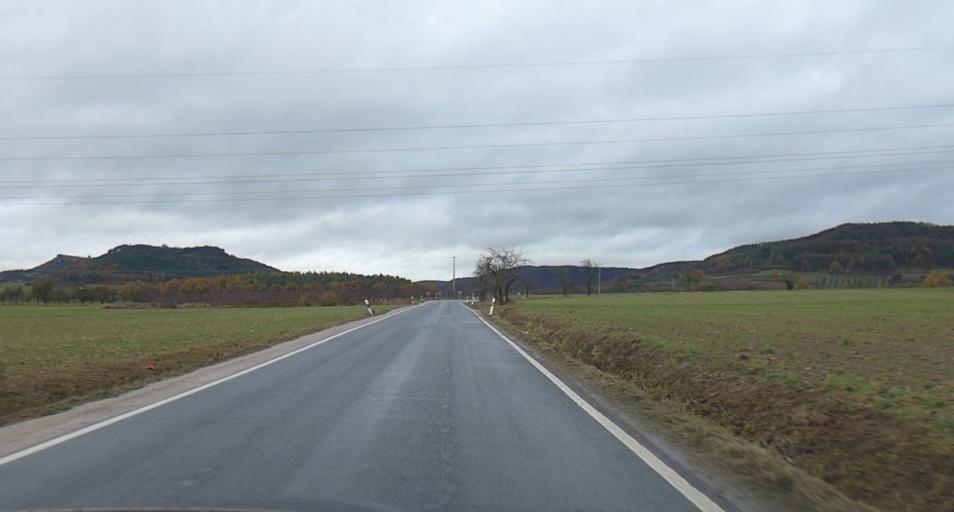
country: DE
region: Bavaria
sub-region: Upper Franconia
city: Kunreuth
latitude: 49.6862
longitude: 11.1644
